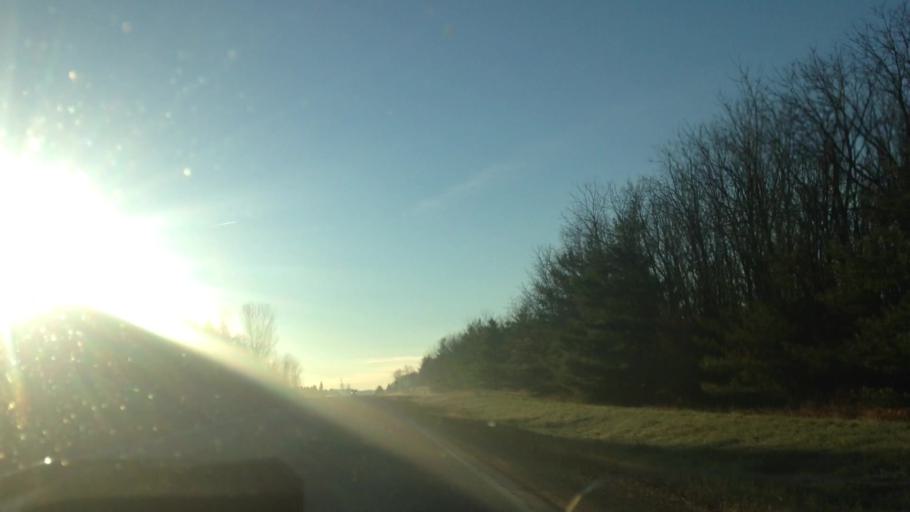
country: US
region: Wisconsin
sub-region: Dodge County
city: Mayville
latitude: 43.4897
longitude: -88.5179
